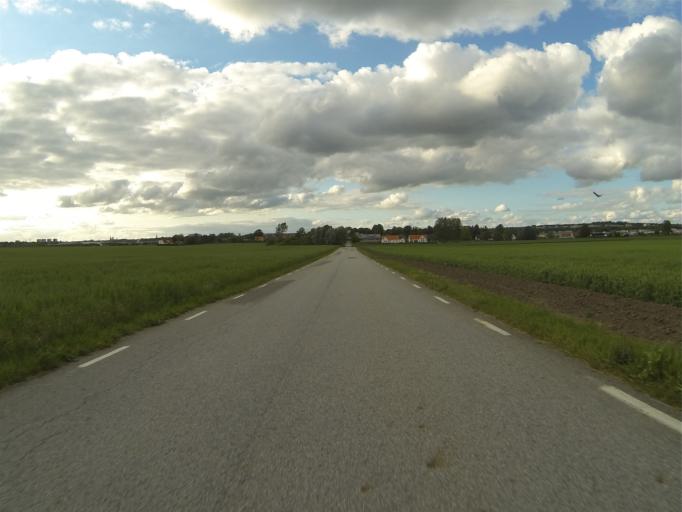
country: SE
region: Skane
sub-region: Lunds Kommun
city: Lund
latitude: 55.6815
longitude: 13.2257
